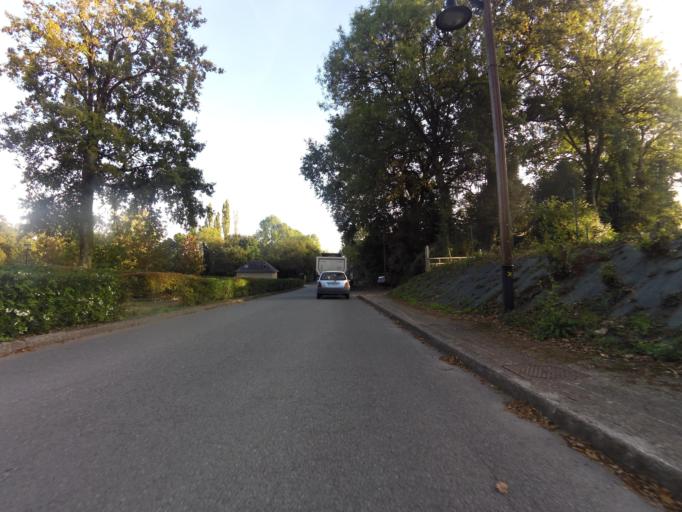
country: FR
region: Brittany
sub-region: Departement du Morbihan
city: Trefflean
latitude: 47.6413
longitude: -2.5993
